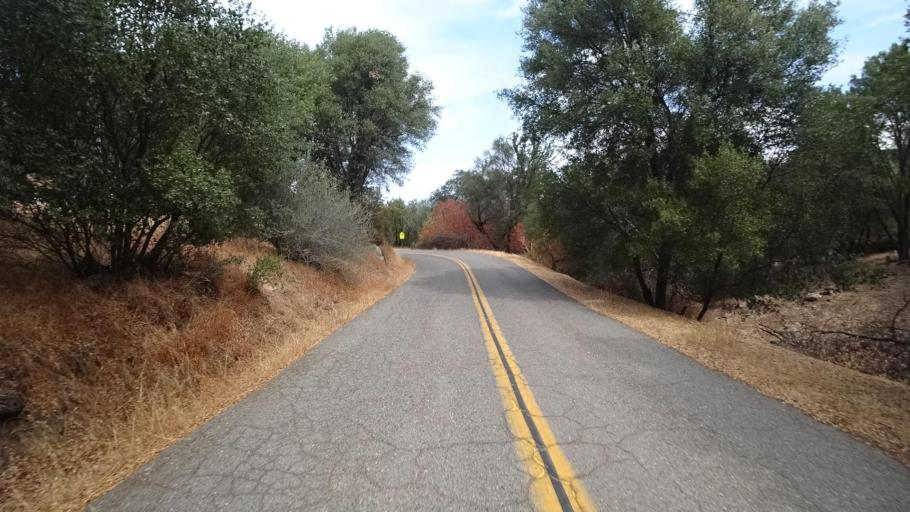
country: US
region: California
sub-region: Mariposa County
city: Midpines
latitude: 37.4496
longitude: -119.8446
